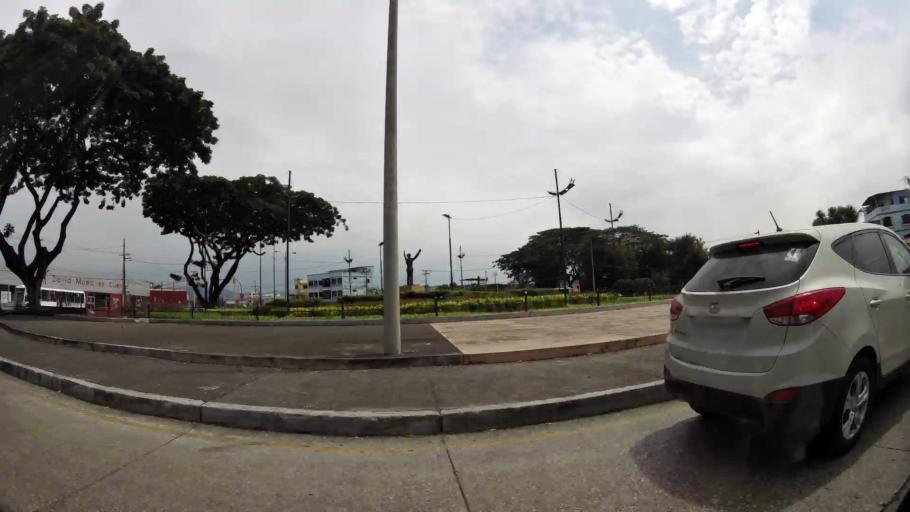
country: EC
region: Guayas
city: Eloy Alfaro
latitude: -2.1417
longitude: -79.8886
